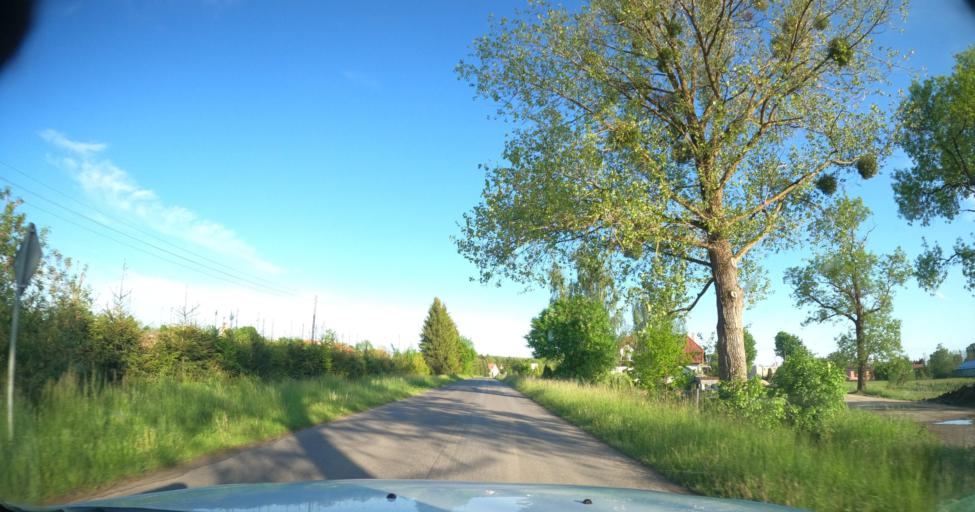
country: PL
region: Warmian-Masurian Voivodeship
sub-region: Powiat braniewski
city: Braniewo
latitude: 54.2722
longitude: 19.9350
